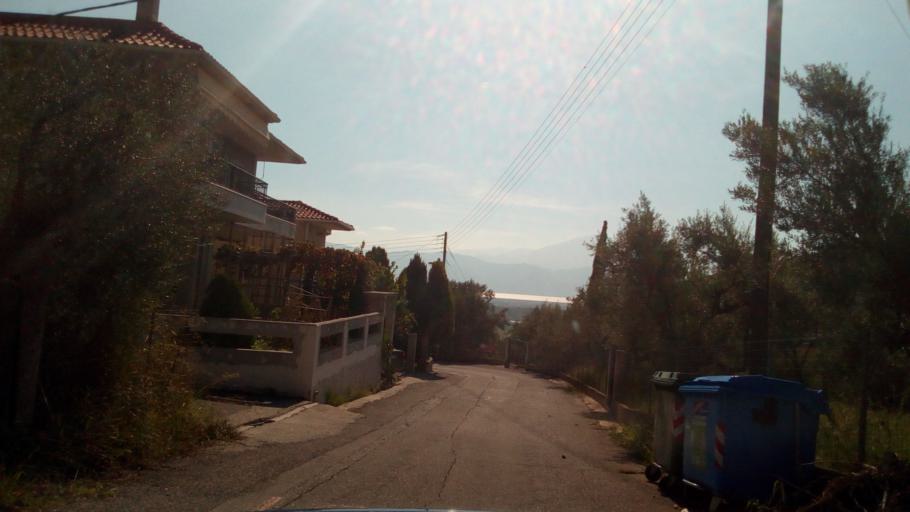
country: GR
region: West Greece
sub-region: Nomos Aitolias kai Akarnanias
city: Nafpaktos
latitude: 38.4185
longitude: 21.8712
